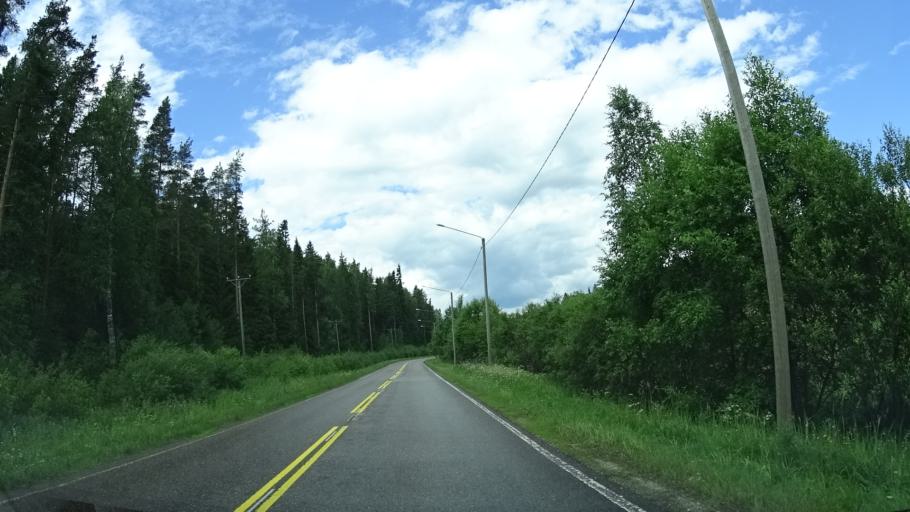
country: FI
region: Uusimaa
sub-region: Helsinki
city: Espoo
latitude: 60.3568
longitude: 24.6441
